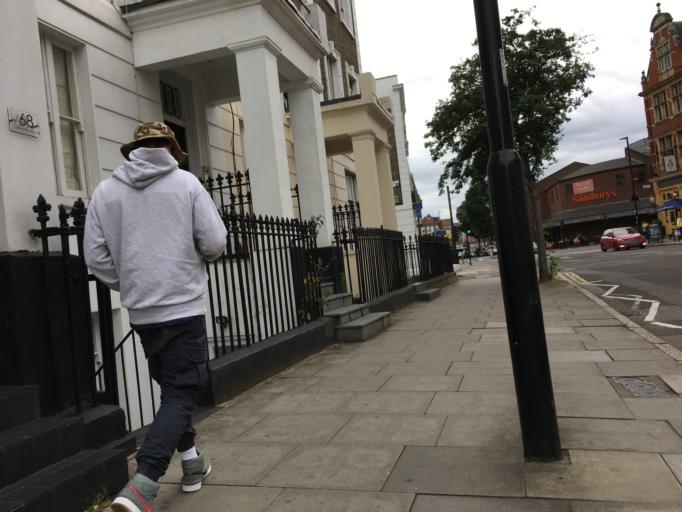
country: GB
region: England
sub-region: Greater London
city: Islington
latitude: 51.5352
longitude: -0.1071
